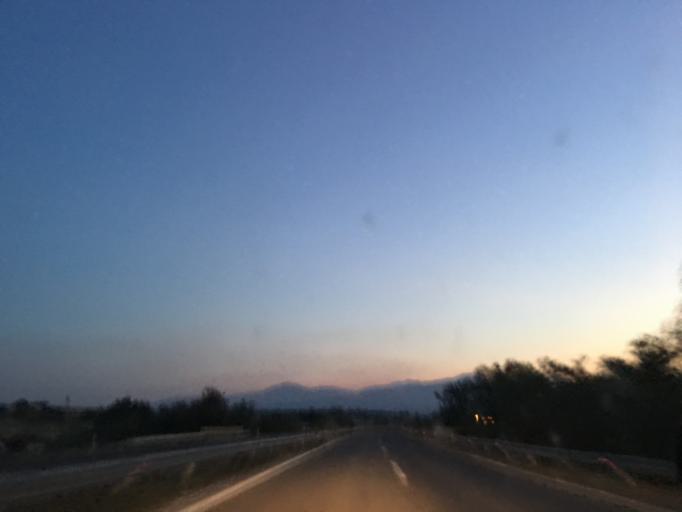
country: MK
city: Miladinovci
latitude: 41.9748
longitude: 21.6498
